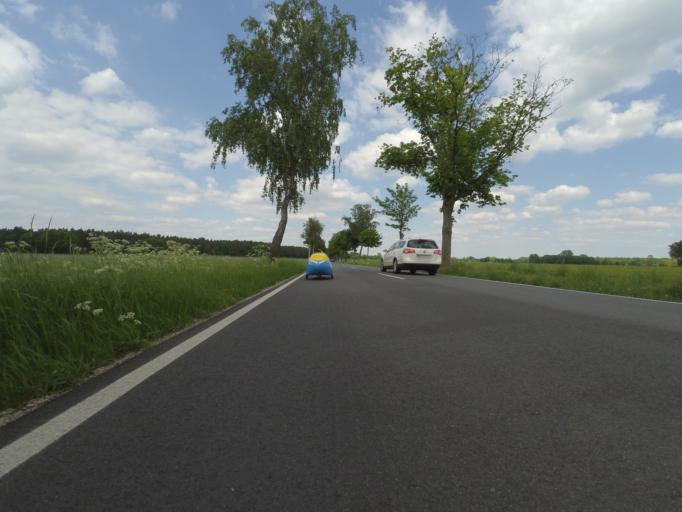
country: DE
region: Lower Saxony
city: Burgdorf
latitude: 52.4721
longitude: 10.0378
